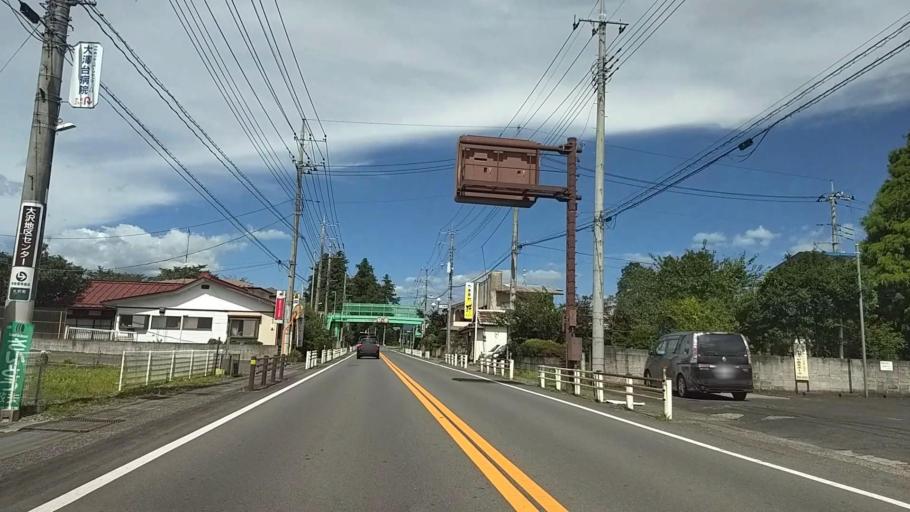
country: JP
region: Tochigi
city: Imaichi
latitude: 36.6954
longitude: 139.7567
